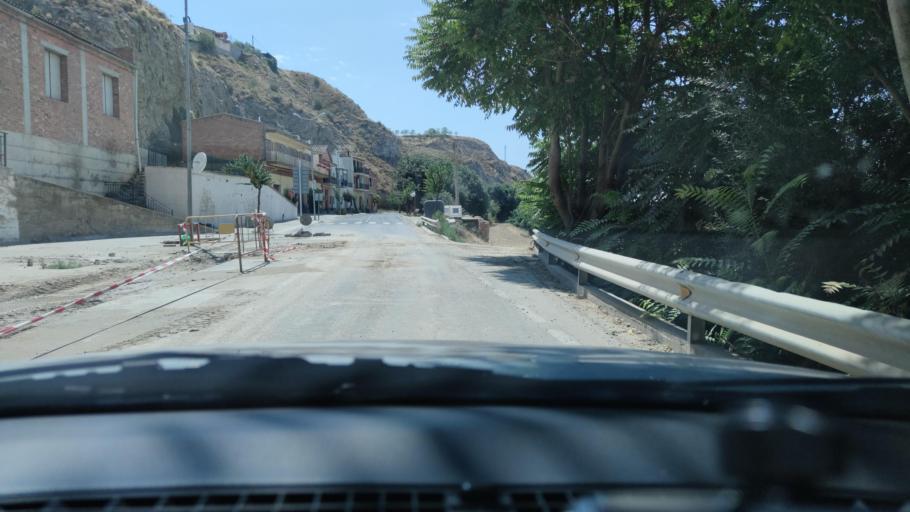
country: ES
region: Catalonia
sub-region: Provincia de Lleida
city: Alfarras
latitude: 41.8496
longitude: 0.5852
